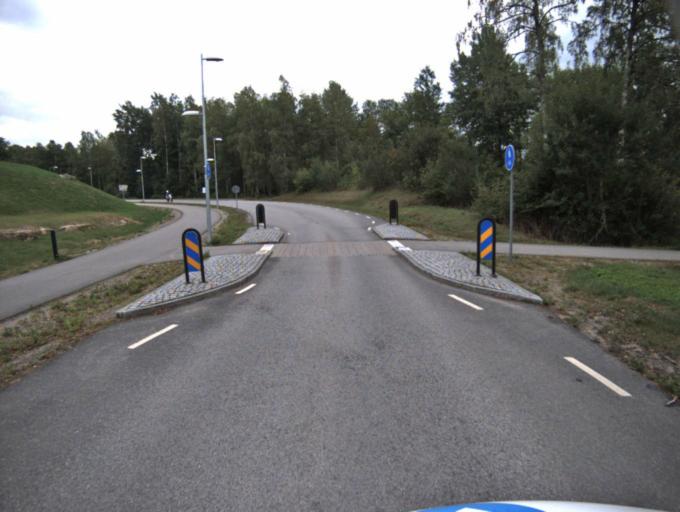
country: SE
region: Vaestra Goetaland
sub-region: Ulricehamns Kommun
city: Ulricehamn
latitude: 57.7859
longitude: 13.4319
